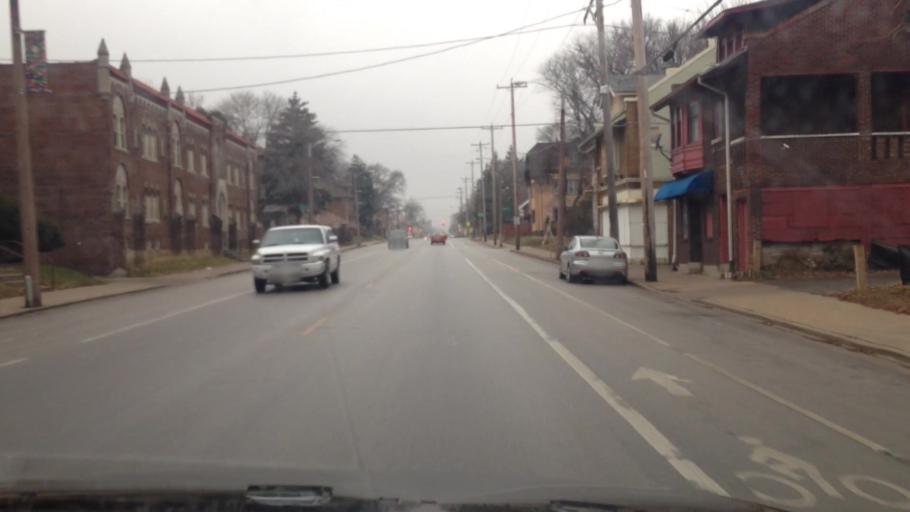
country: US
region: Wisconsin
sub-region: Milwaukee County
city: Wauwatosa
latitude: 43.0680
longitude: -87.9635
